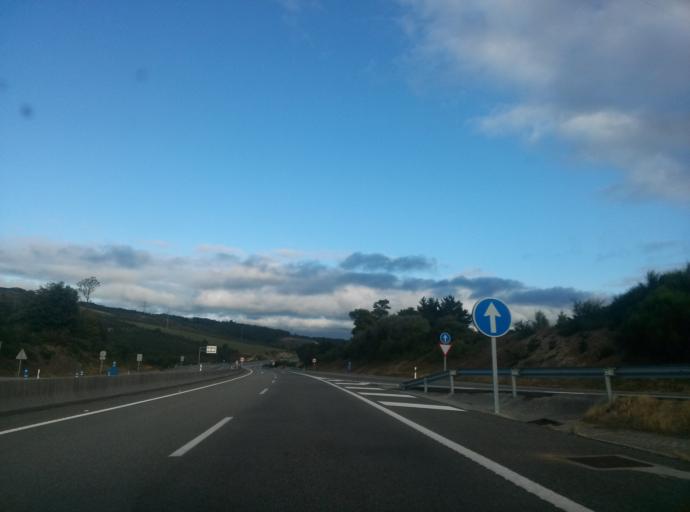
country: ES
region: Galicia
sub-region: Provincia de Lugo
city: Vilalba
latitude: 43.3527
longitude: -7.7439
